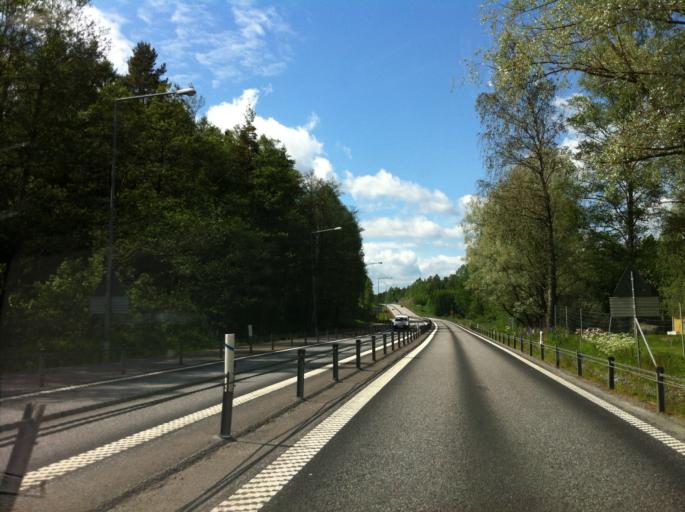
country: SE
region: Vaermland
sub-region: Grums Kommun
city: Slottsbron
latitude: 59.3153
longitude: 13.0962
